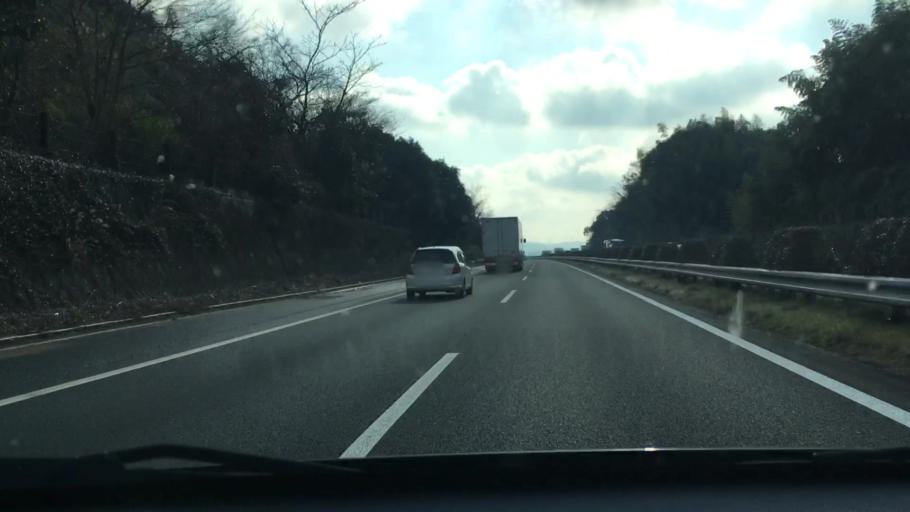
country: JP
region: Kumamoto
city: Kumamoto
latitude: 32.7258
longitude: 130.7724
